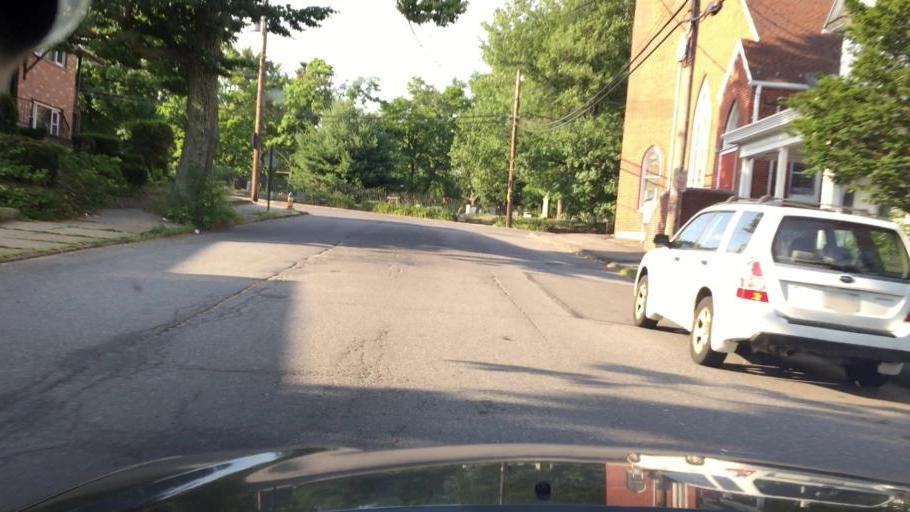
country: US
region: Pennsylvania
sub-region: Luzerne County
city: Hazleton
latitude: 40.9570
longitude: -75.9798
